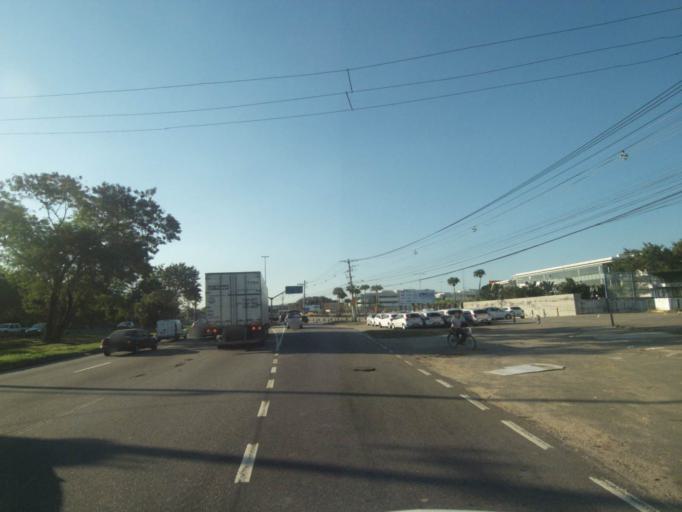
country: BR
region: Rio de Janeiro
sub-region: Rio De Janeiro
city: Rio de Janeiro
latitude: -22.9662
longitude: -43.3571
